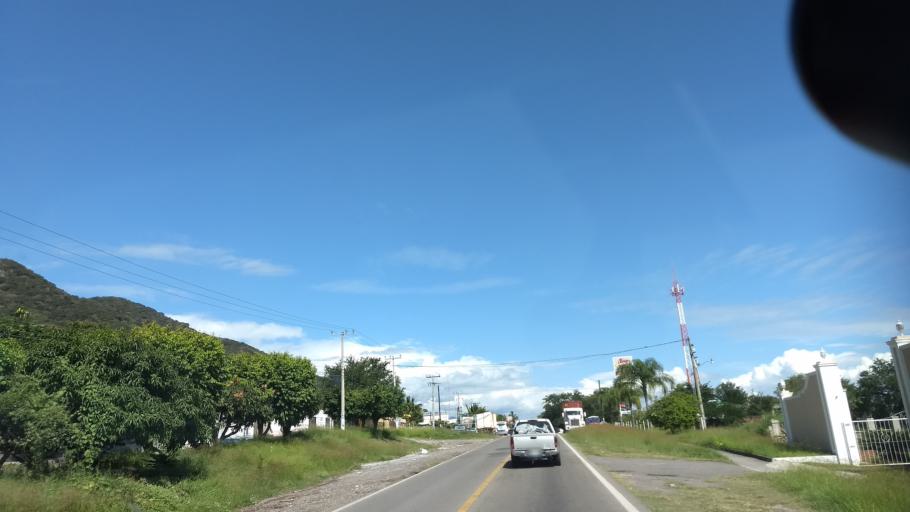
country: MX
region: Jalisco
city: Tuxpan
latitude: 19.5535
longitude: -103.3901
